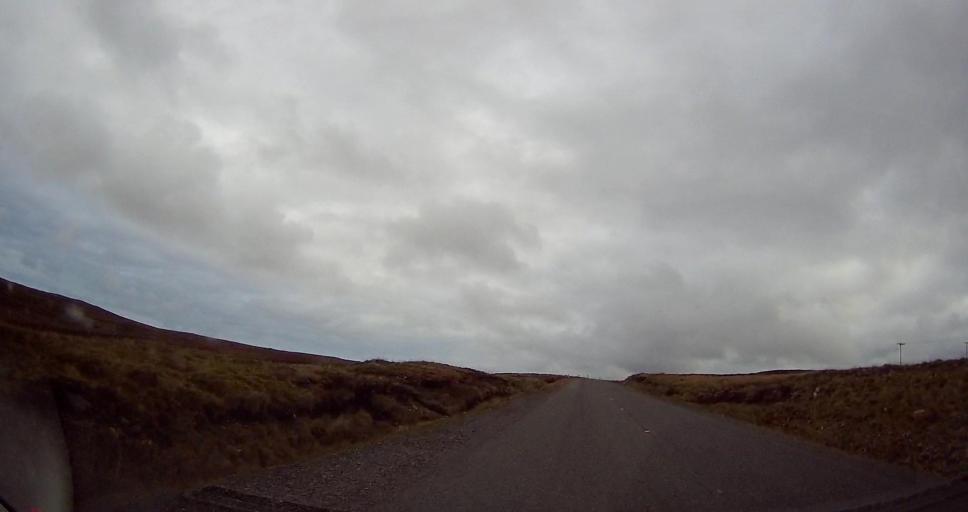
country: GB
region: Scotland
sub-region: Shetland Islands
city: Shetland
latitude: 60.6227
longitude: -1.0739
